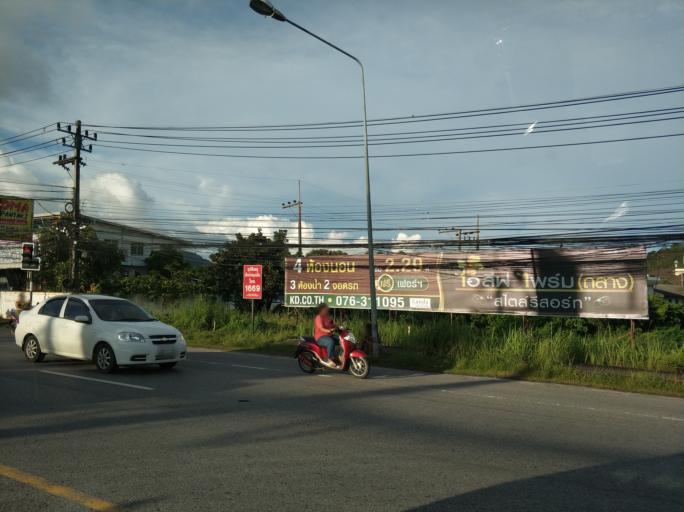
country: TH
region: Phuket
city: Wichit
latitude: 7.8958
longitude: 98.3640
